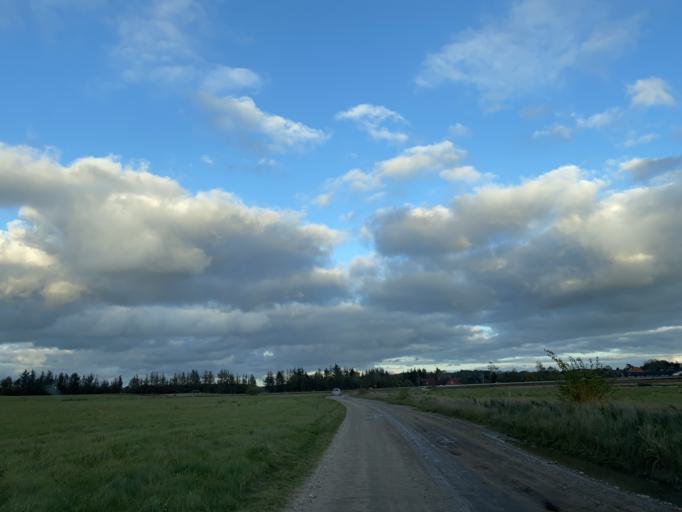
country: DK
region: Central Jutland
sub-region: Silkeborg Kommune
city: Svejbaek
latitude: 56.1819
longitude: 9.6355
